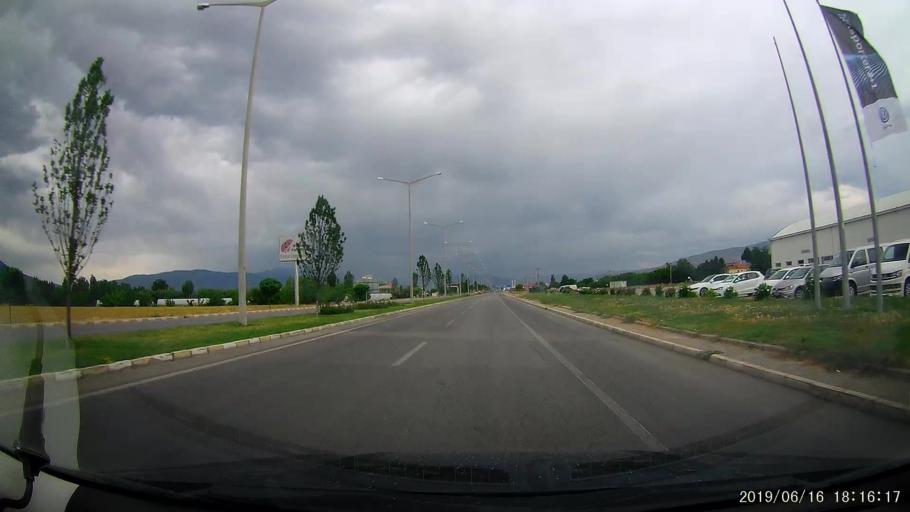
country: TR
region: Erzincan
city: Erzincan
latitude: 39.7275
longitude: 39.5499
